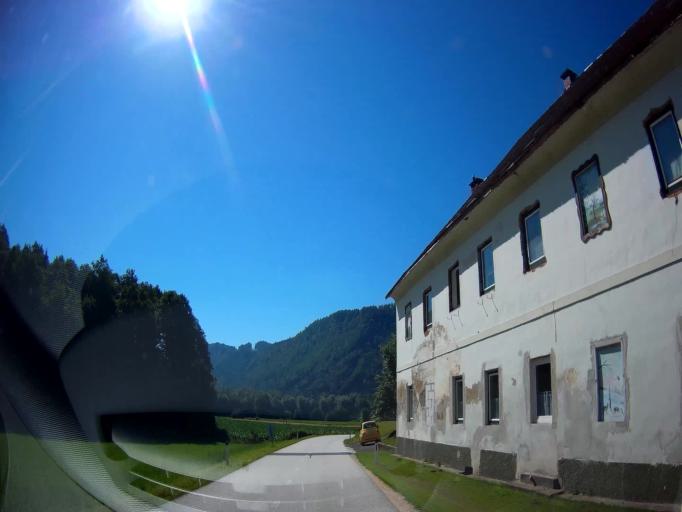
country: AT
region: Carinthia
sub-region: Politischer Bezirk Klagenfurt Land
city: Grafenstein
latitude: 46.6115
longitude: 14.4396
